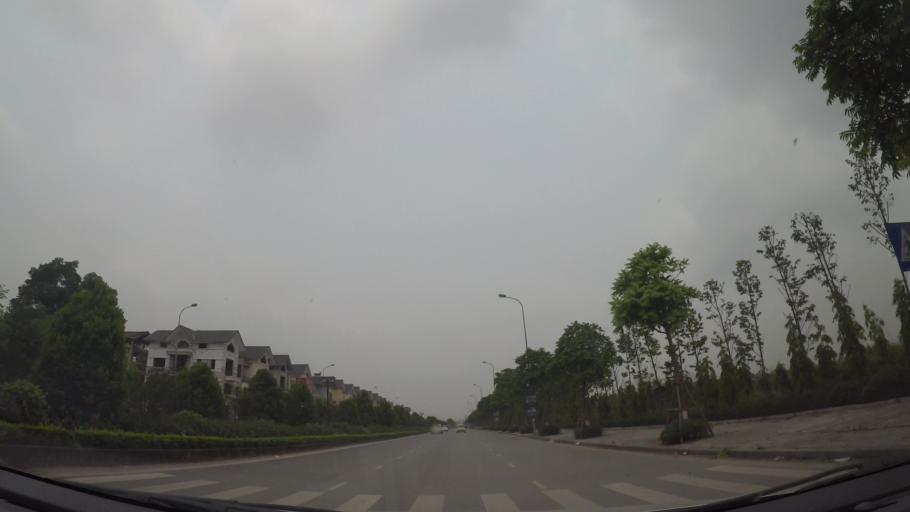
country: VN
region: Ha Noi
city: Ha Dong
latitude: 20.9790
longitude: 105.7626
